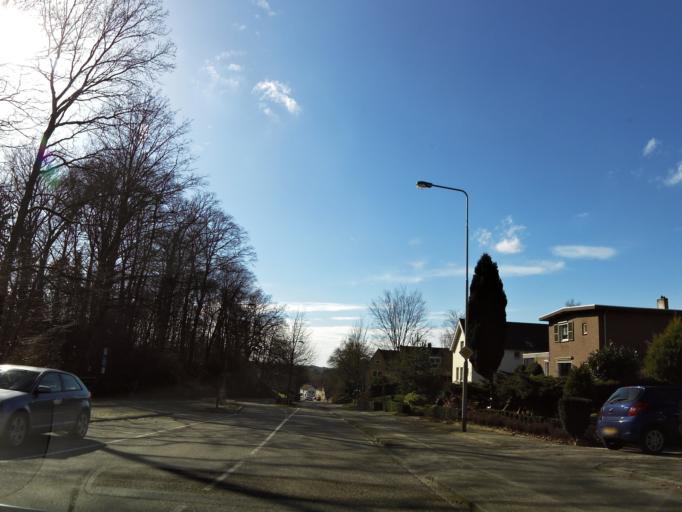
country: NL
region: Limburg
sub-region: Gemeente Simpelveld
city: Simpelveld
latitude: 50.8375
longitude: 5.9864
